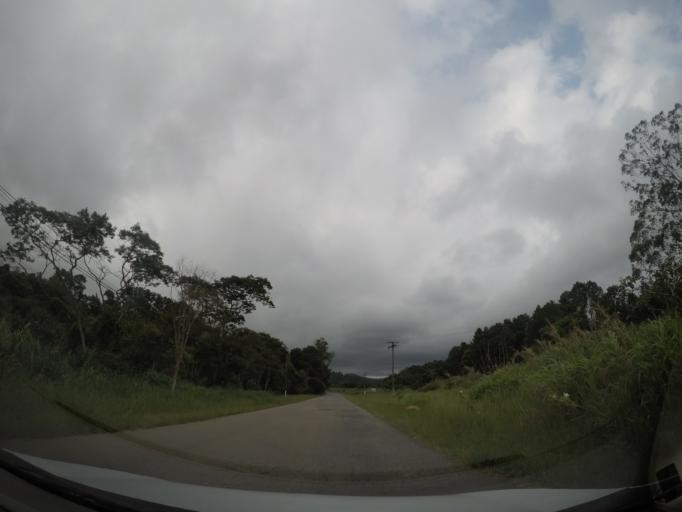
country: BR
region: Sao Paulo
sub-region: Aruja
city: Aruja
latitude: -23.3851
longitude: -46.3569
